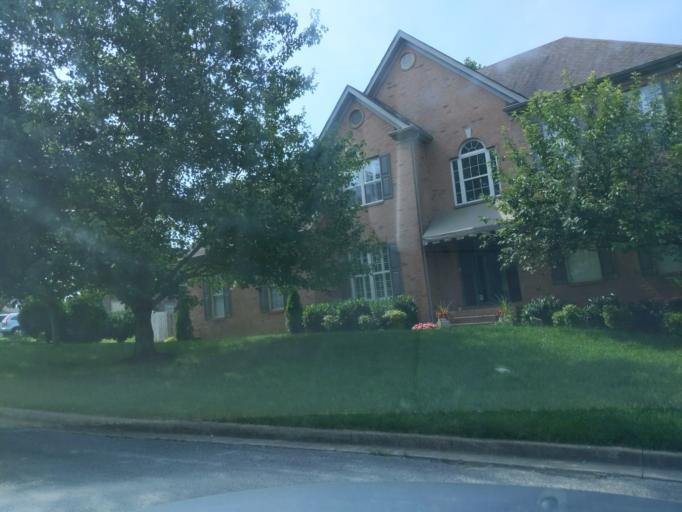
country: US
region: Tennessee
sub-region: Williamson County
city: Brentwood Estates
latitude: 36.0330
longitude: -86.7546
